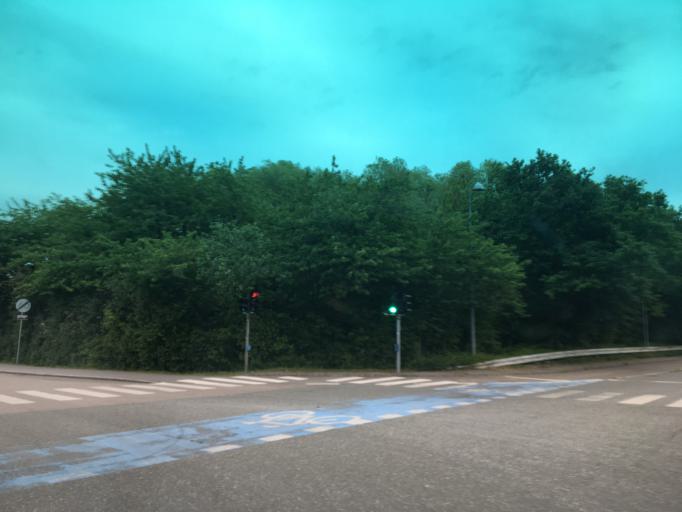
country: DK
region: Capital Region
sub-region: Vallensbaek Kommune
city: Vallensbaek
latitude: 55.6432
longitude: 12.3565
